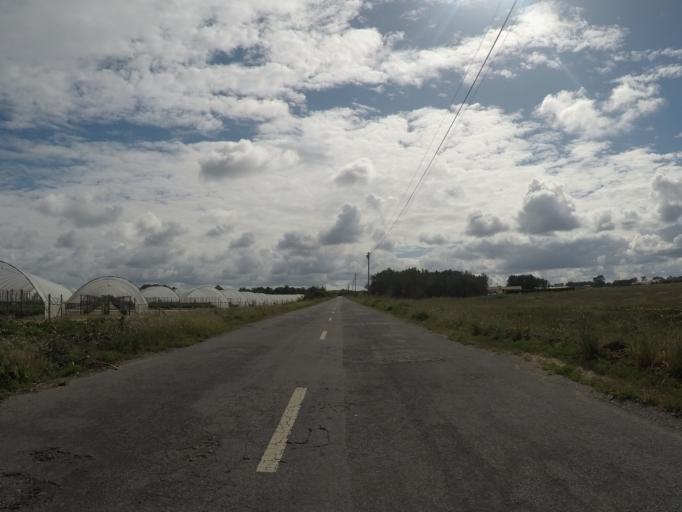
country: PT
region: Beja
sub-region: Odemira
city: Sao Teotonio
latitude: 37.4787
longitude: -8.7814
